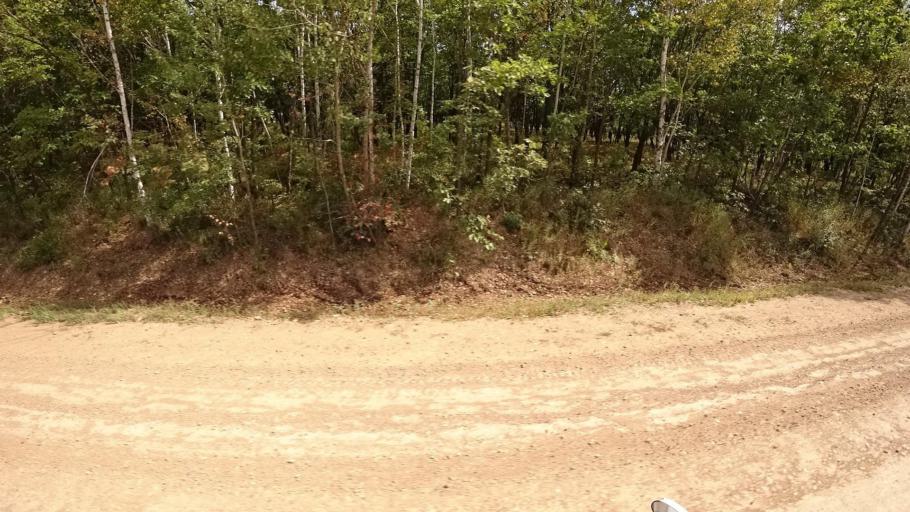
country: RU
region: Primorskiy
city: Yakovlevka
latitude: 44.7301
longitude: 133.6094
